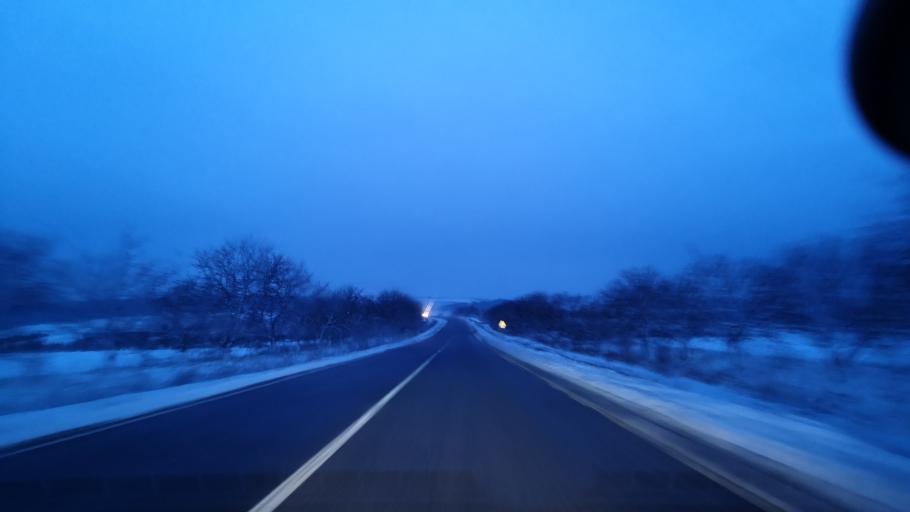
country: MD
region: Rezina
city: Saharna
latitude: 47.6127
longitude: 28.8311
